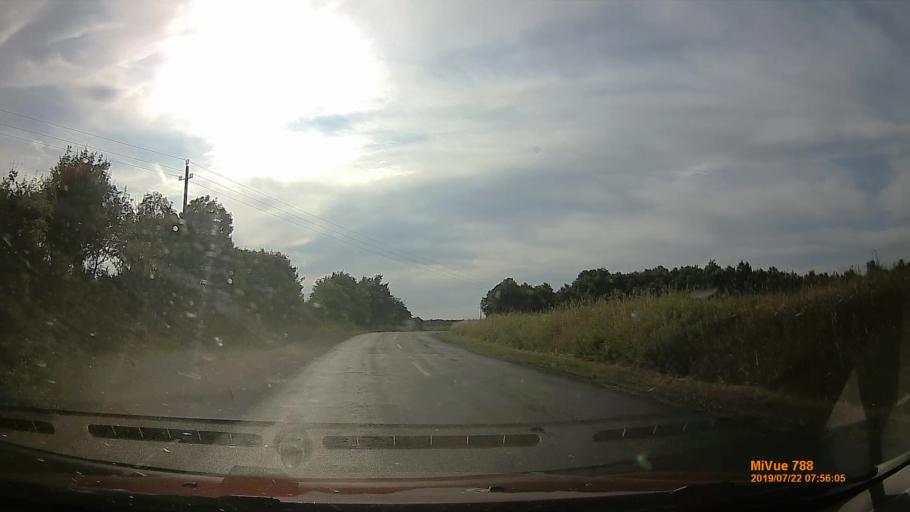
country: HU
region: Veszprem
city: Ajka
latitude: 47.0299
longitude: 17.5642
